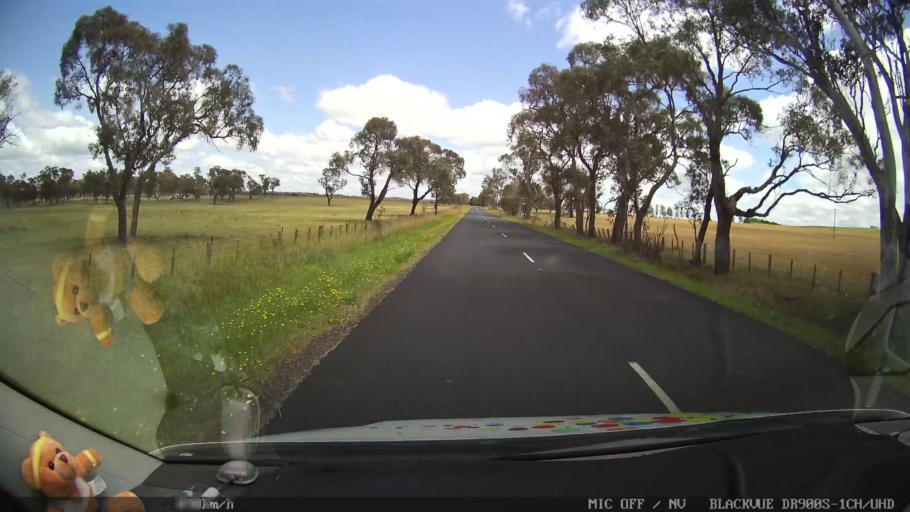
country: AU
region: New South Wales
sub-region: Glen Innes Severn
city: Glen Innes
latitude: -29.6505
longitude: 151.6931
